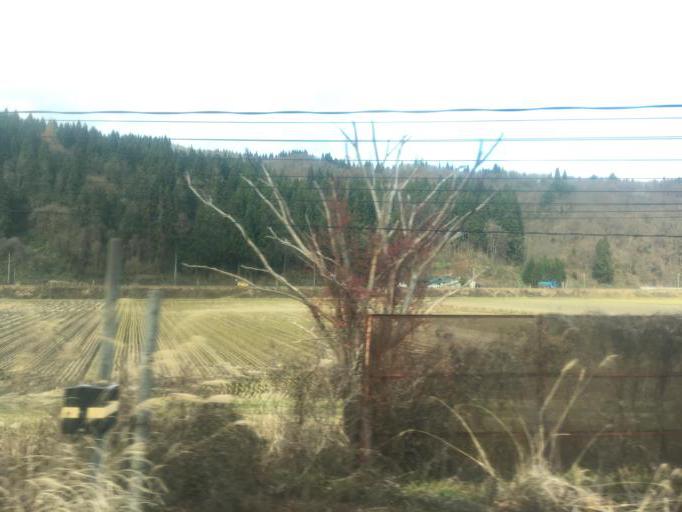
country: JP
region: Akita
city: Takanosu
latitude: 40.2159
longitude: 140.3150
